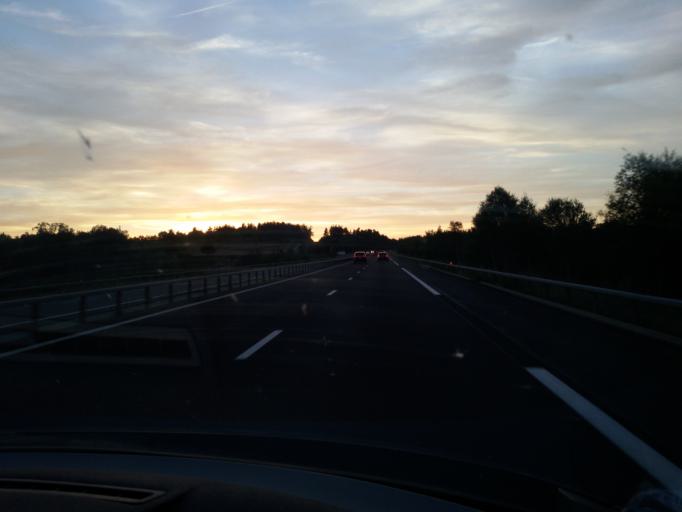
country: FR
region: Languedoc-Roussillon
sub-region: Departement de la Lozere
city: Le Malzieu-Ville
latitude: 44.8164
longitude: 3.2804
